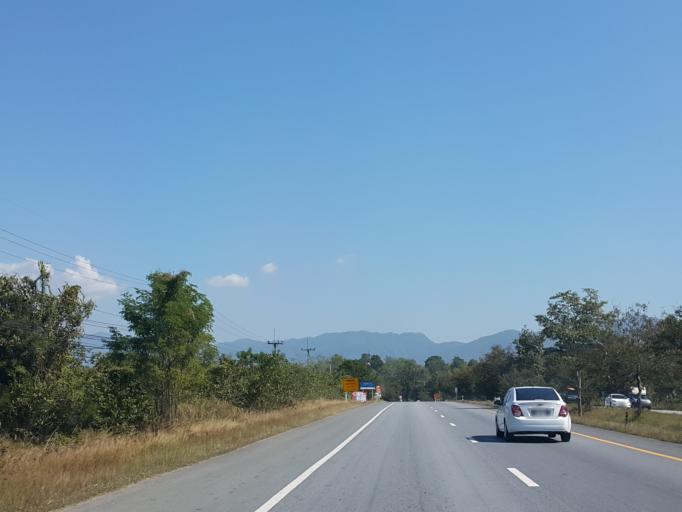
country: TH
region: Lampang
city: Sop Prap
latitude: 17.8623
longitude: 99.3248
